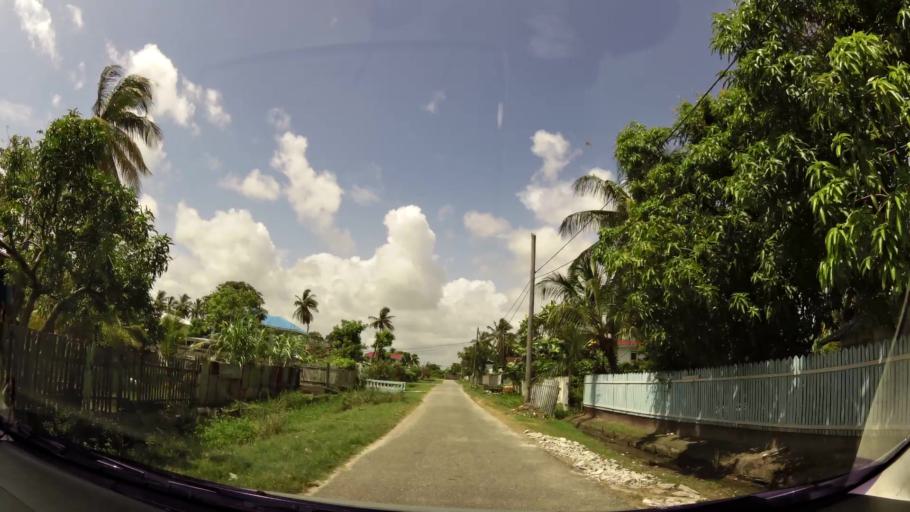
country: GY
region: Demerara-Mahaica
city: Mahaica Village
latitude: 6.7637
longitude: -58.0106
